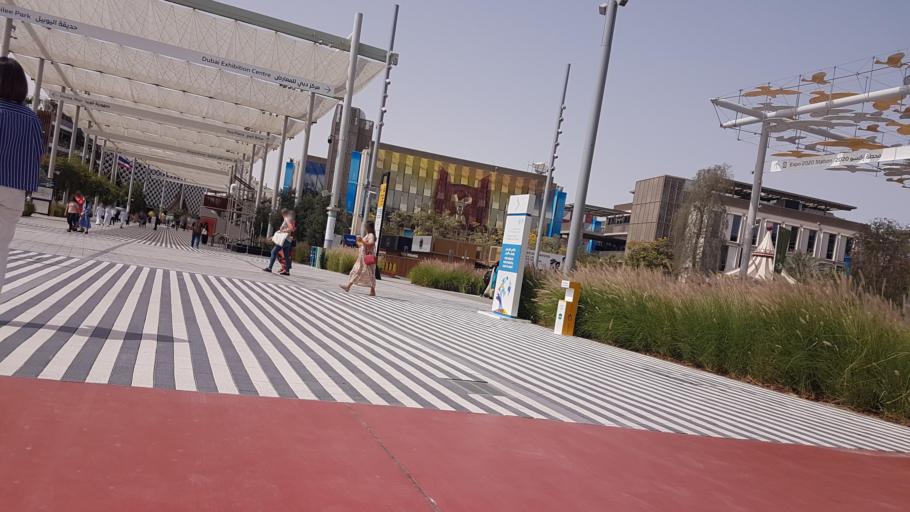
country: AE
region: Dubai
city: Dubai
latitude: 24.9588
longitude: 55.1495
